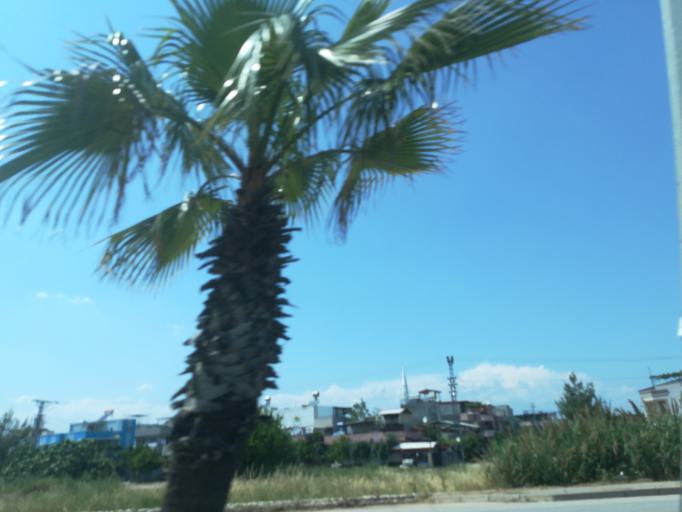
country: TR
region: Adana
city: Yuregir
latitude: 37.0126
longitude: 35.3973
